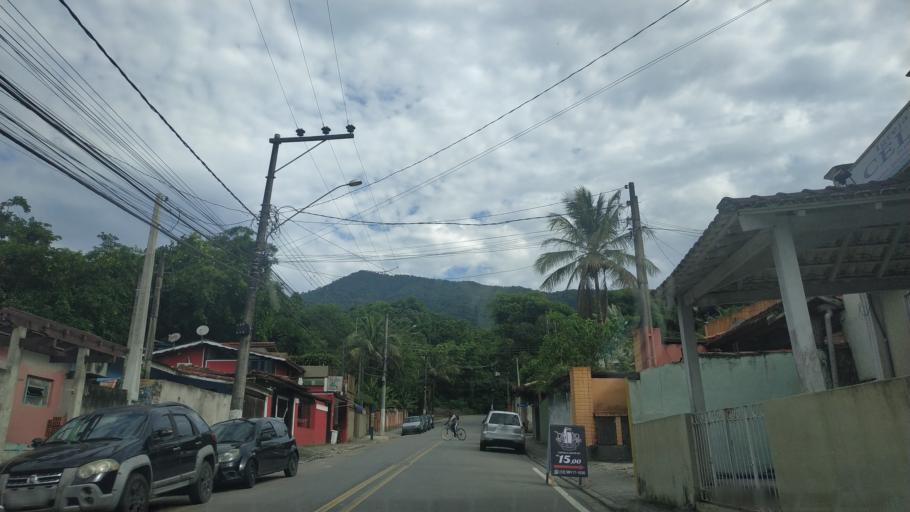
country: BR
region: Sao Paulo
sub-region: Ilhabela
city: Ilhabela
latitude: -23.8215
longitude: -45.3539
